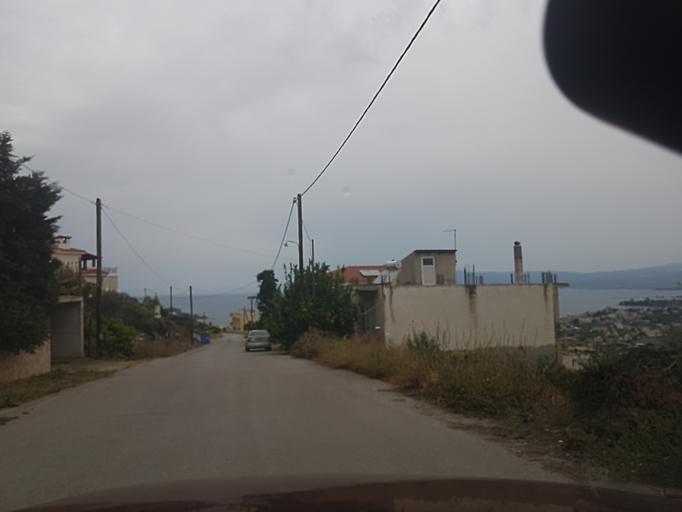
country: GR
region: Central Greece
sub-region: Nomos Evvoias
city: Chalkida
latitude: 38.4608
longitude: 23.6276
